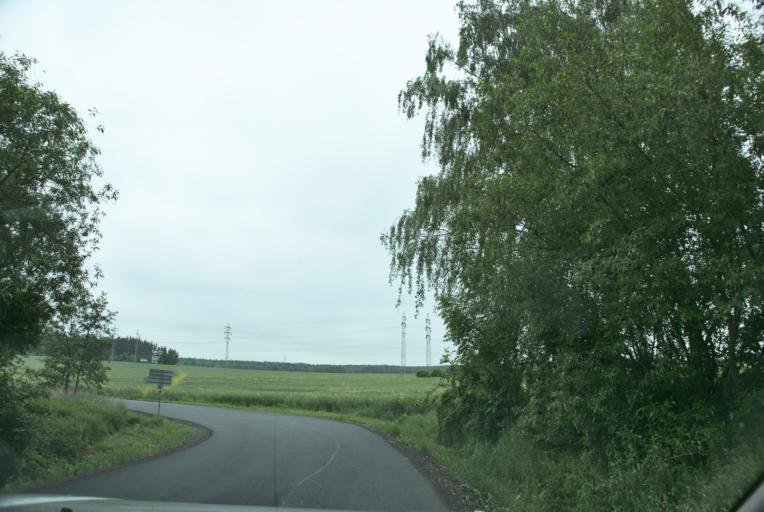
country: CZ
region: Plzensky
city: Kralovice
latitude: 49.9853
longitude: 13.4667
